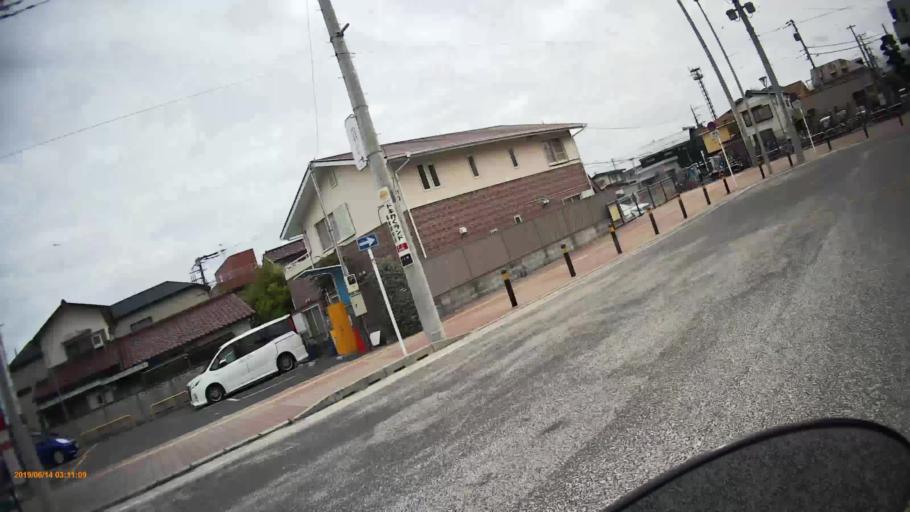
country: JP
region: Kanagawa
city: Fujisawa
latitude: 35.4121
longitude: 139.4649
